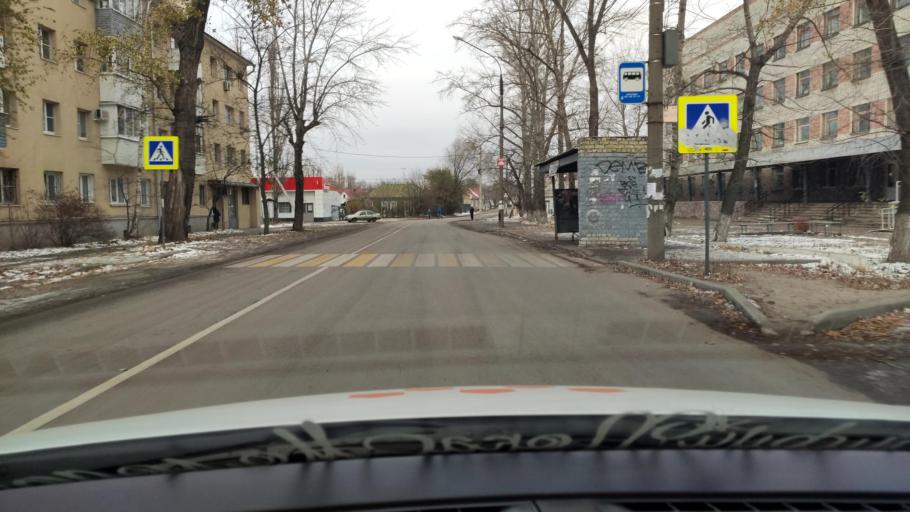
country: RU
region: Voronezj
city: Somovo
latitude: 51.7319
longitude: 39.2790
